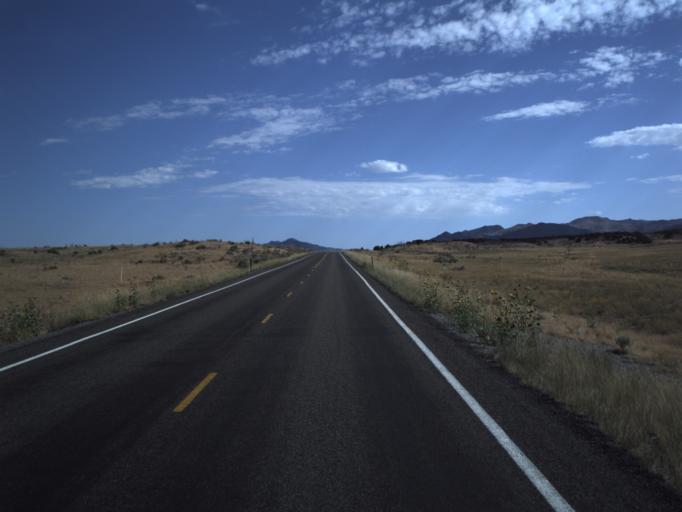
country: US
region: Utah
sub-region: Juab County
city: Mona
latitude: 39.7495
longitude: -112.1842
